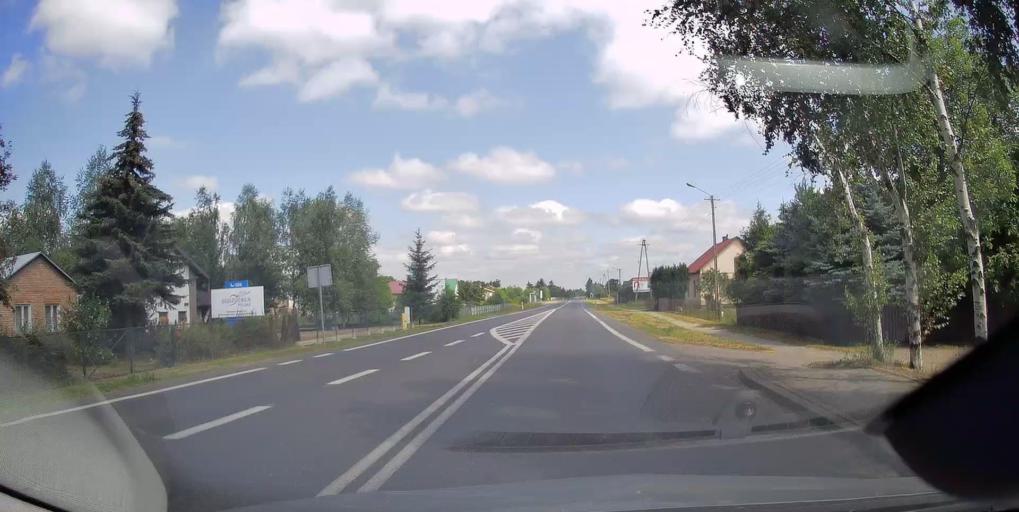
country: PL
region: Subcarpathian Voivodeship
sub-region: Powiat mielecki
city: Przeclaw
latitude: 50.1708
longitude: 21.4907
